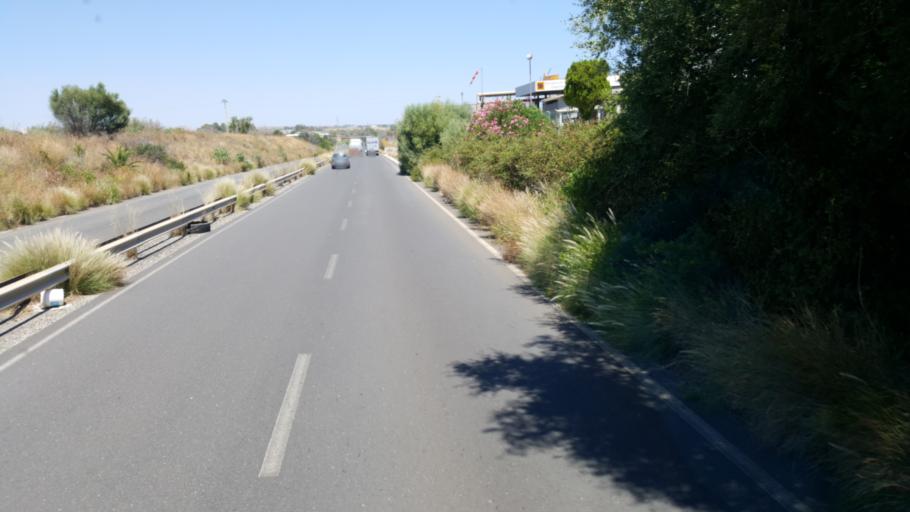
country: IT
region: Sicily
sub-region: Provincia di Siracusa
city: Melilli
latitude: 37.2056
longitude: 15.1594
